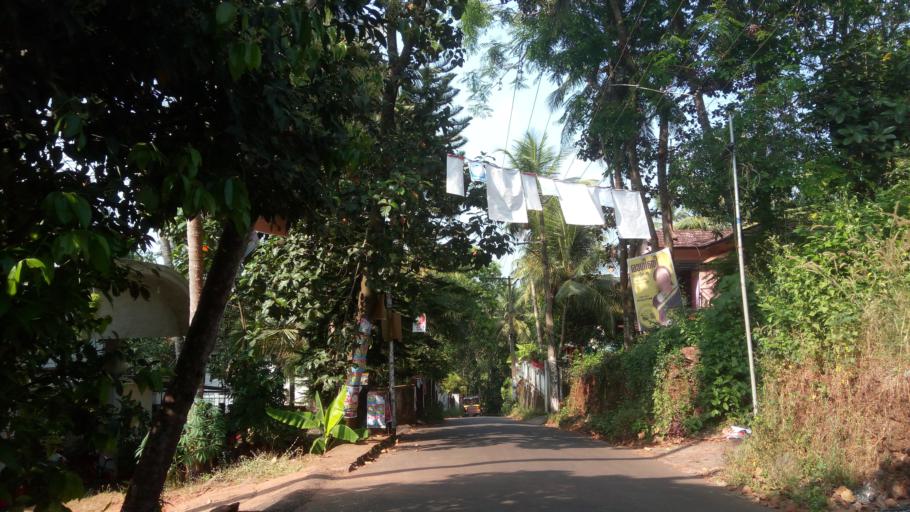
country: IN
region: Kerala
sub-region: Malappuram
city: Malappuram
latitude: 10.9929
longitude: 75.9997
